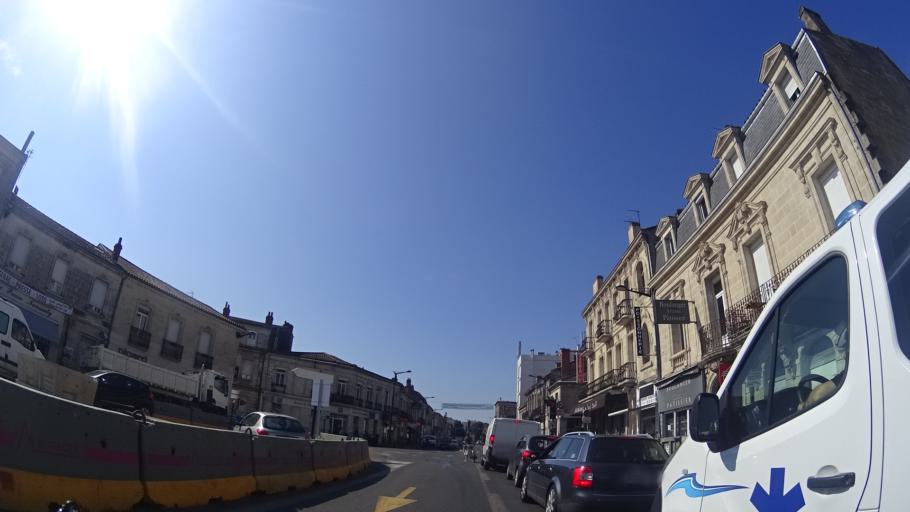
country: FR
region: Aquitaine
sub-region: Departement de la Gironde
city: Bordeaux
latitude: 44.8198
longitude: -0.5724
